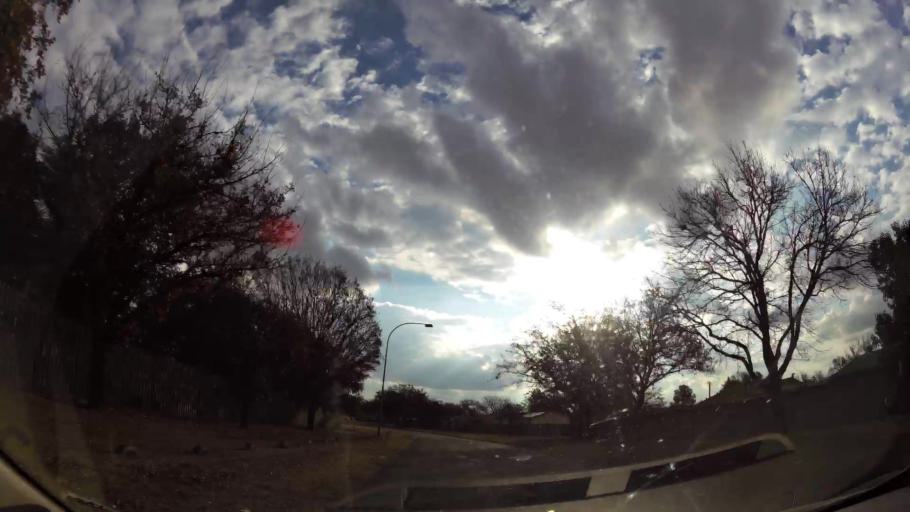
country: ZA
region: Orange Free State
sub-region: Fezile Dabi District Municipality
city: Sasolburg
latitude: -26.8260
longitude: 27.8169
